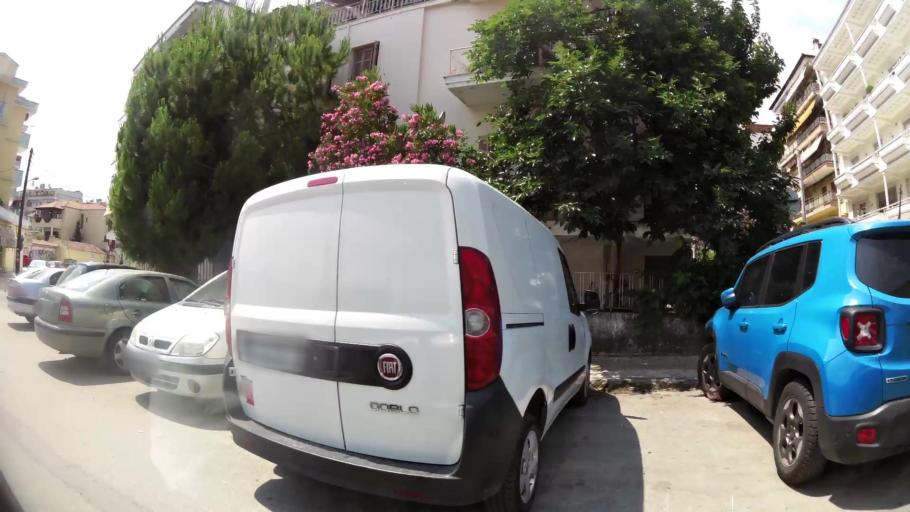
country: GR
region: Central Macedonia
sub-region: Nomos Imathias
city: Veroia
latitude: 40.5220
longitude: 22.2069
